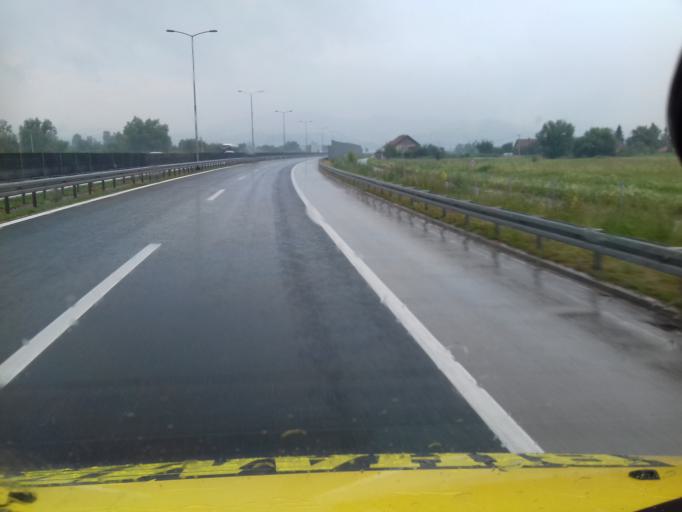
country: BA
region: Federation of Bosnia and Herzegovina
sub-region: Kanton Sarajevo
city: Sarajevo
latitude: 43.8543
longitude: 18.3123
